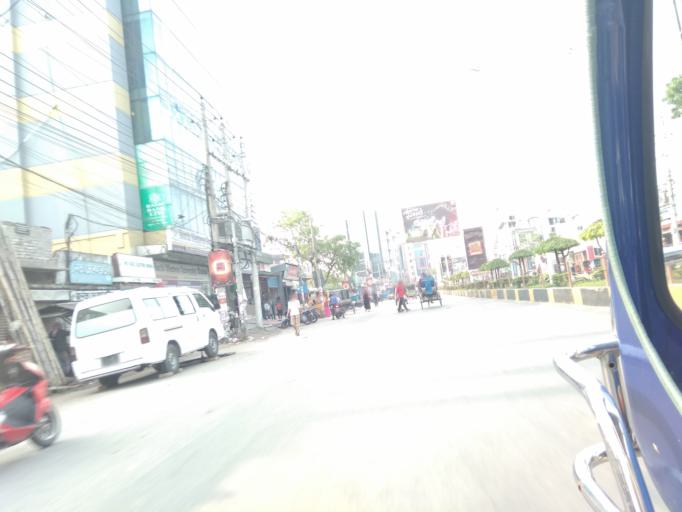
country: BD
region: Khulna
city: Khulna
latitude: 22.8169
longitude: 89.5538
